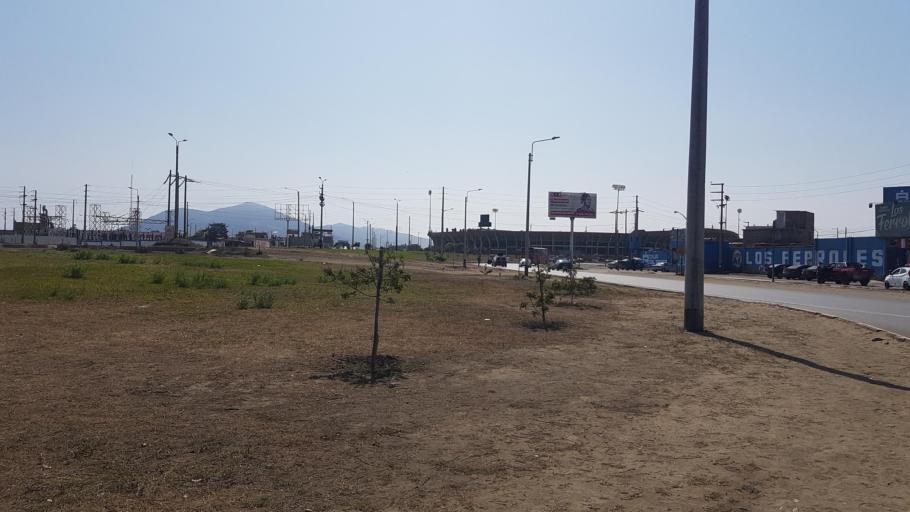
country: PE
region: Ancash
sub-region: Provincia de Santa
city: Chimbote
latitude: -9.1031
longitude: -78.5587
